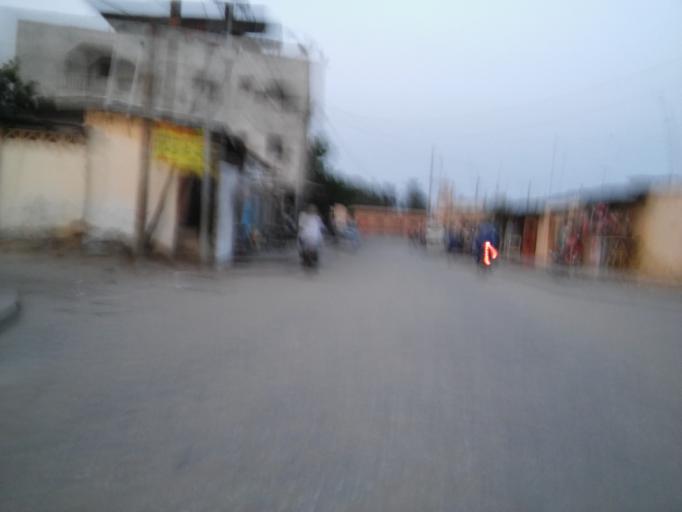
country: BJ
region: Atlantique
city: Abomey-Calavi
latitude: 6.3910
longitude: 2.3499
